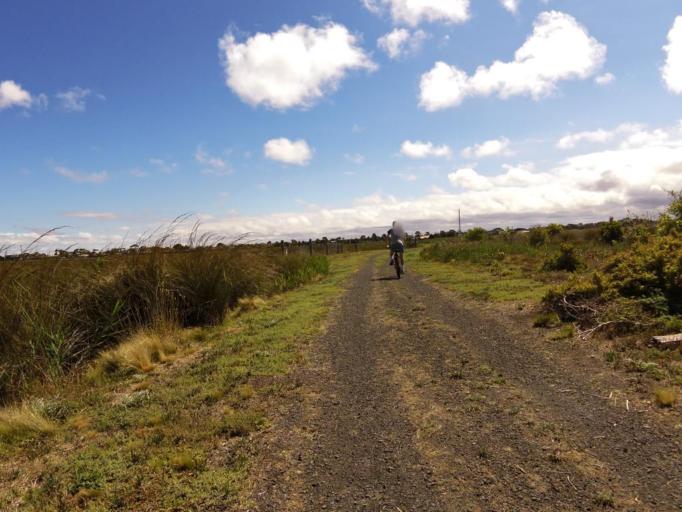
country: AU
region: Victoria
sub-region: Hobsons Bay
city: Altona Meadows
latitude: -37.8654
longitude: 144.7968
